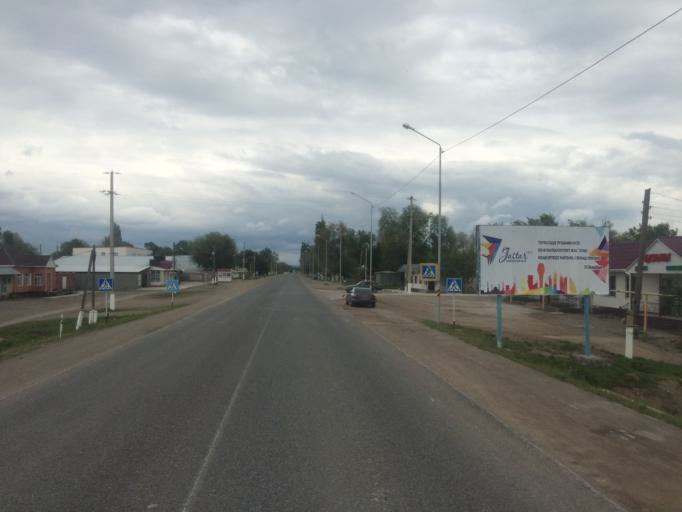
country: KZ
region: Zhambyl
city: Georgiyevka
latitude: 43.2273
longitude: 74.3937
